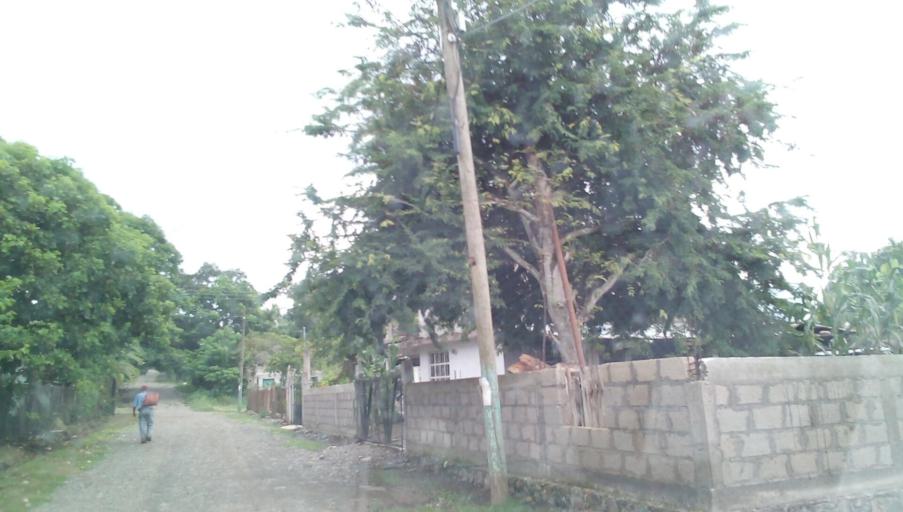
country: MX
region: Veracruz
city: Tepetzintla
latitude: 21.1266
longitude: -97.8559
